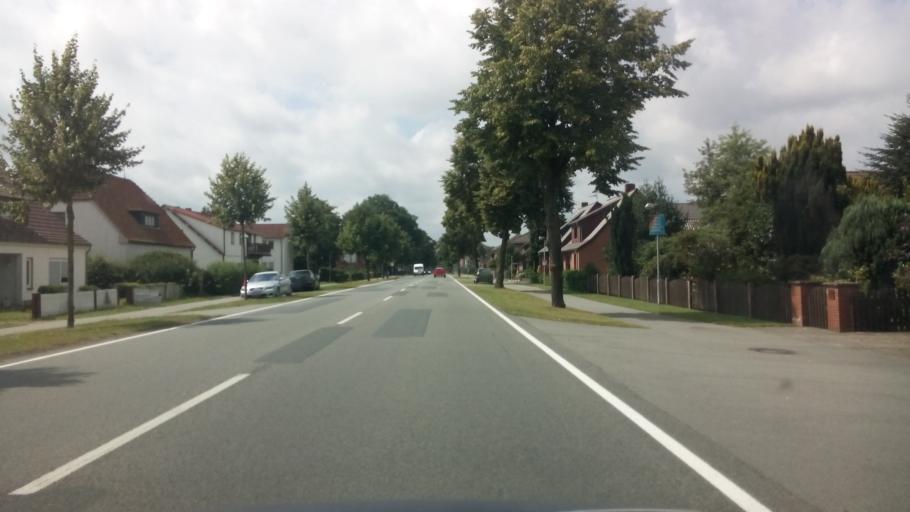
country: DE
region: Lower Saxony
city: Barnstorf
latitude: 52.7186
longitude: 8.5270
